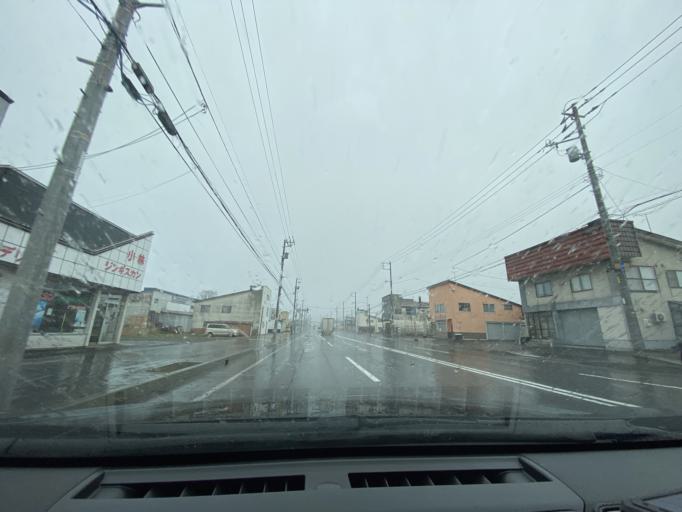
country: JP
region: Hokkaido
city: Takikawa
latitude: 43.6260
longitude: 141.9414
